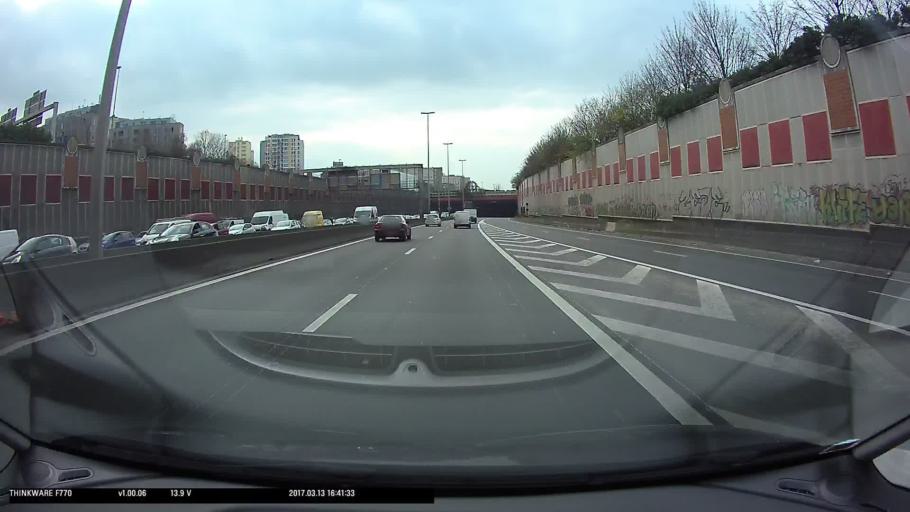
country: FR
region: Ile-de-France
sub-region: Departement de Seine-Saint-Denis
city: Bobigny
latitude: 48.9066
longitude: 2.4580
